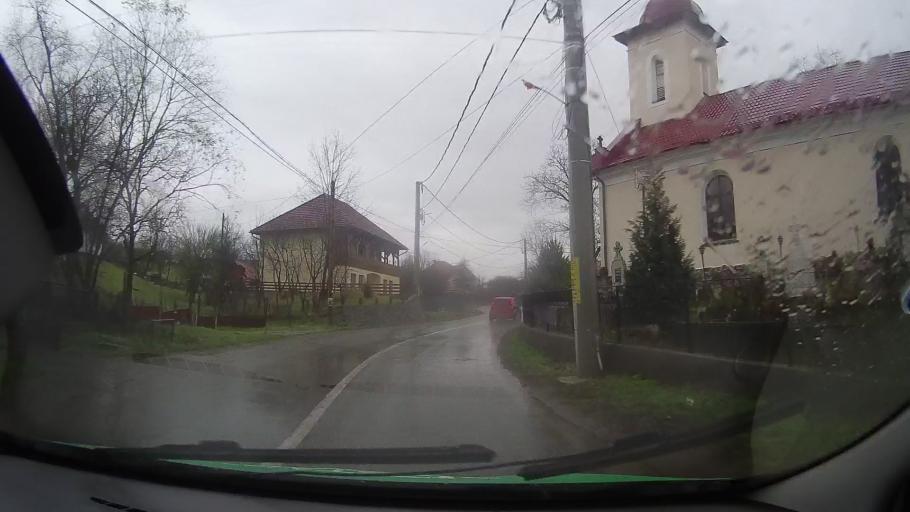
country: RO
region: Mures
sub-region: Comuna Vatava
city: Vatava
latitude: 46.9403
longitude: 24.7663
